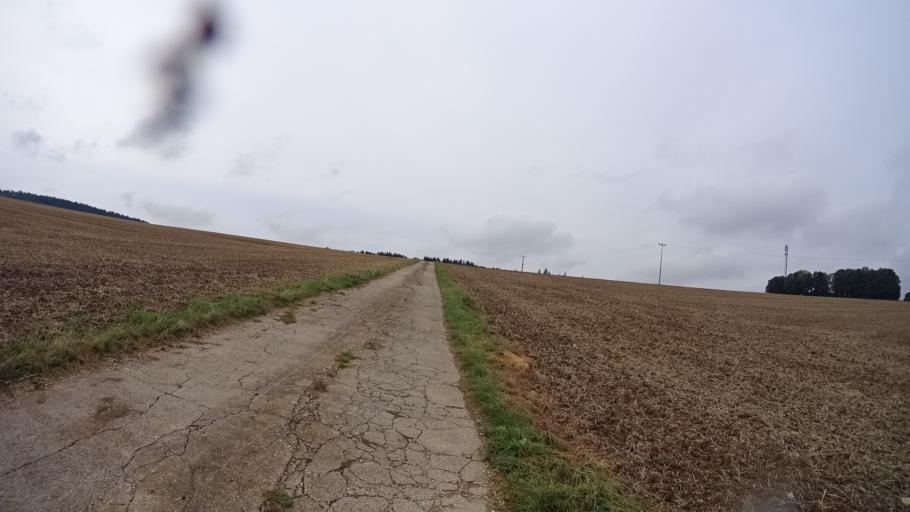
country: DE
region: Bavaria
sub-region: Upper Bavaria
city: Bohmfeld
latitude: 48.8536
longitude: 11.3571
